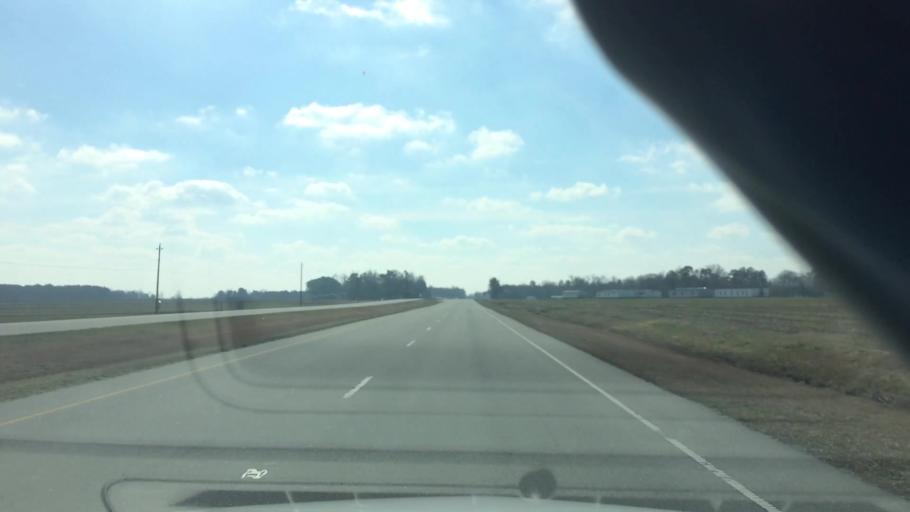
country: US
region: North Carolina
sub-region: Duplin County
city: Beulaville
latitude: 35.0990
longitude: -77.7243
